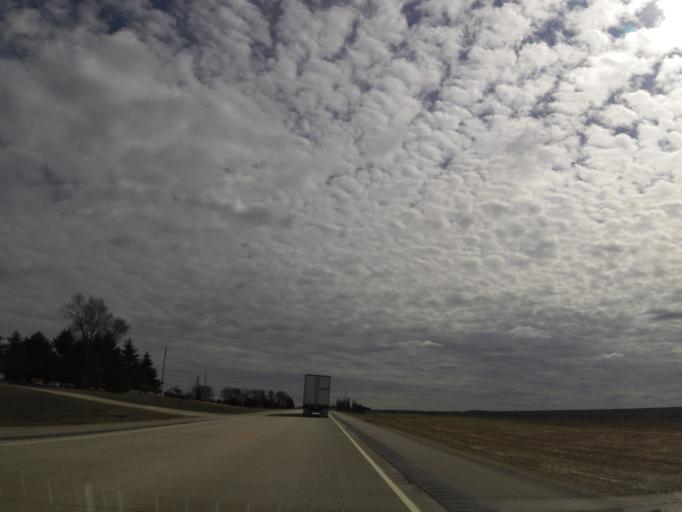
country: US
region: Minnesota
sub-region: Fillmore County
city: Spring Valley
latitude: 43.6574
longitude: -92.3896
